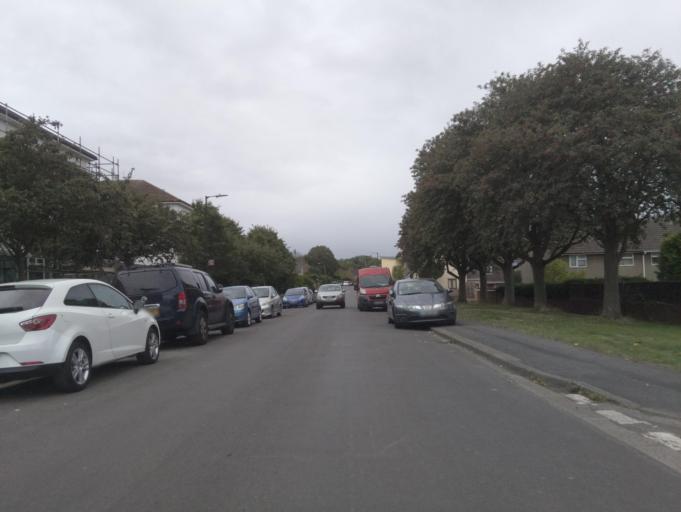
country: GB
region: England
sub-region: North Somerset
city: Easton-in-Gordano
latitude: 51.5012
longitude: -2.6573
